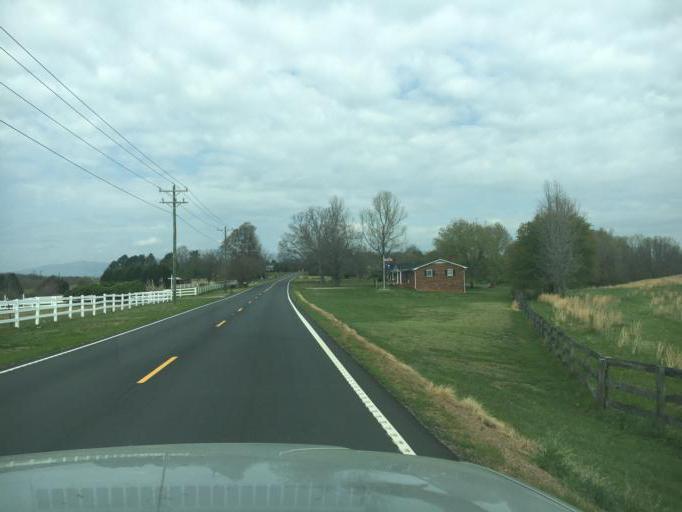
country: US
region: South Carolina
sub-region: Spartanburg County
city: Inman Mills
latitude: 35.0710
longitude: -82.1771
